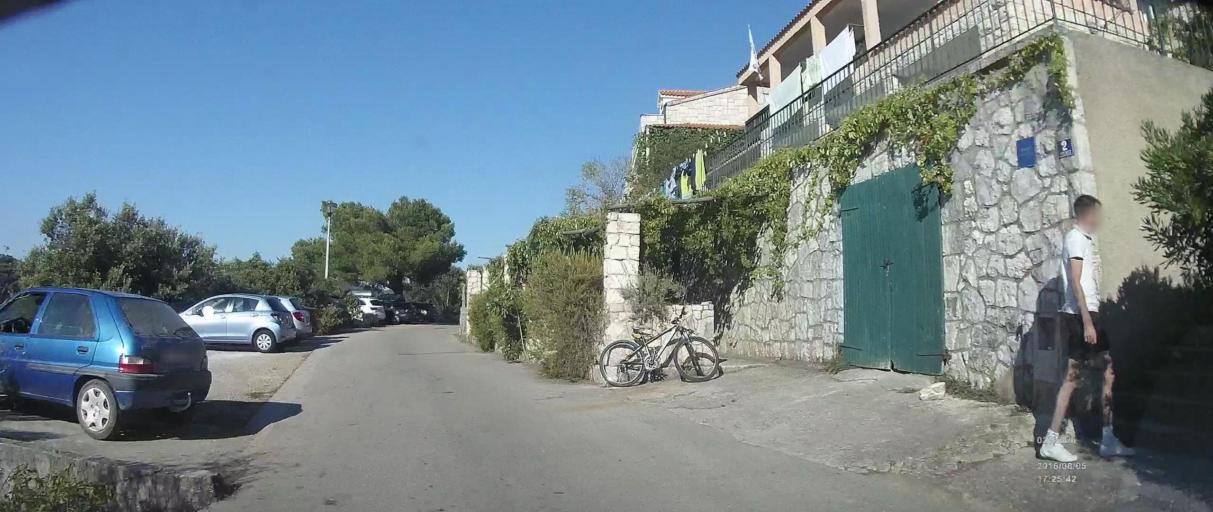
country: HR
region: Dubrovacko-Neretvanska
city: Blato
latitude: 42.7875
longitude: 17.3843
